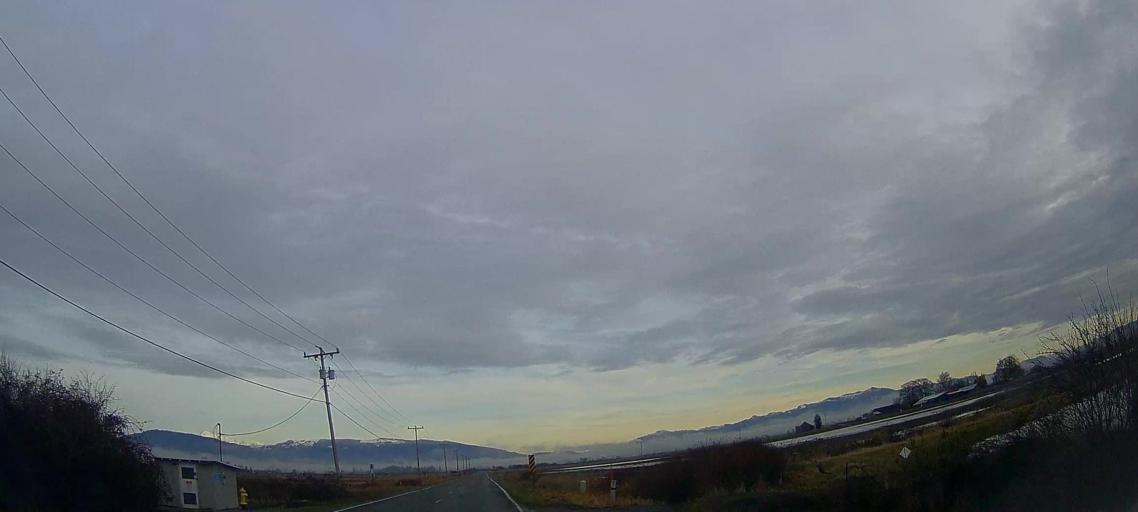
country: US
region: Washington
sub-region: Skagit County
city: Anacortes
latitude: 48.5477
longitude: -122.4815
